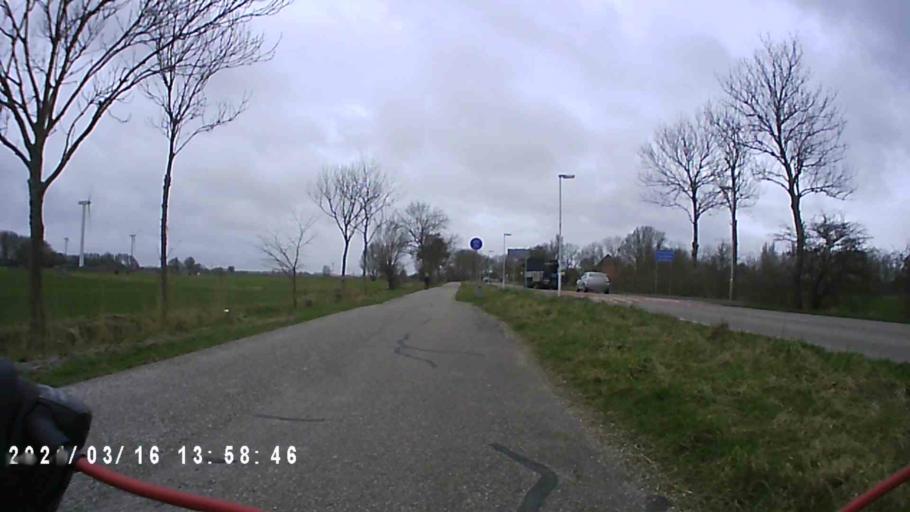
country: NL
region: Friesland
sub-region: Gemeente Franekeradeel
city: Sexbierum
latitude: 53.1837
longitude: 5.5003
